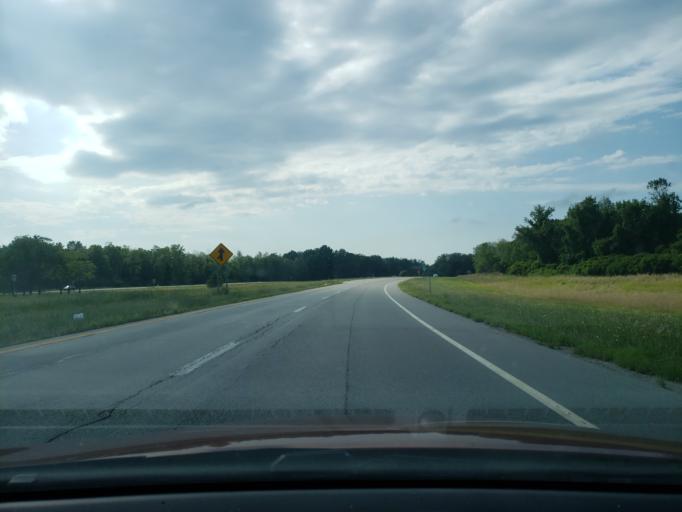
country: US
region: New York
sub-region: Monroe County
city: Greece
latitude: 43.2723
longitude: -77.6862
